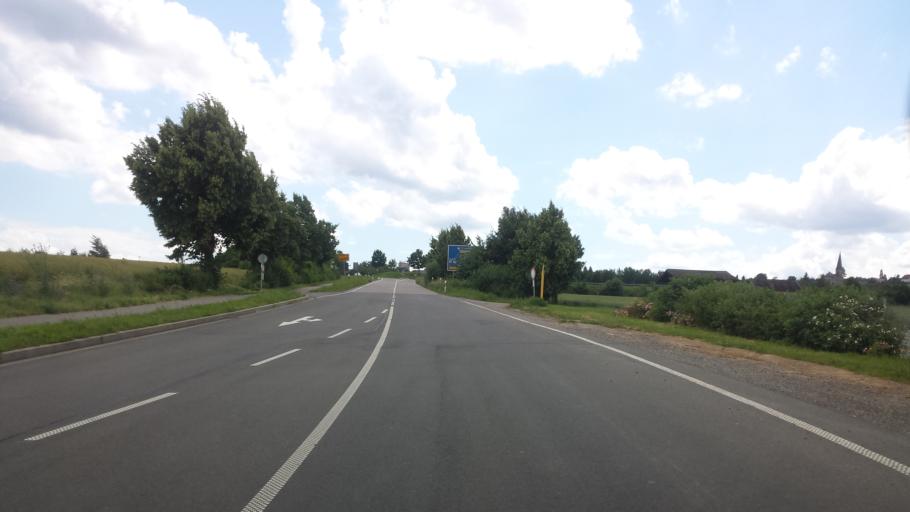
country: DE
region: Rheinland-Pfalz
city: Hettenleidelheim
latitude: 49.5308
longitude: 8.0661
